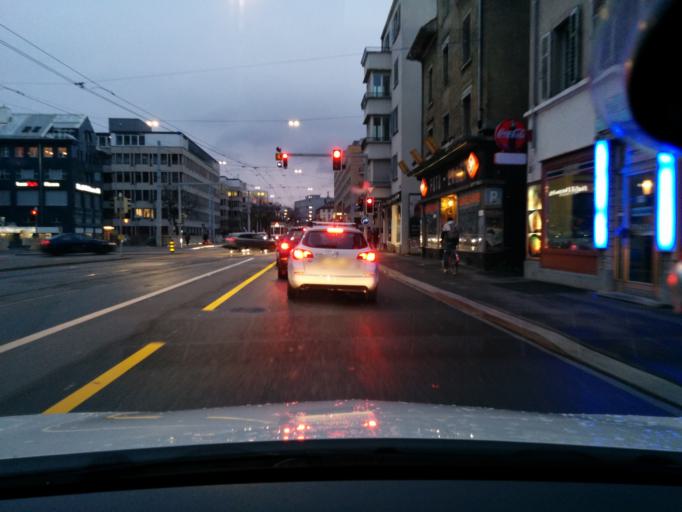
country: CH
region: Zurich
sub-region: Bezirk Zuerich
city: Aussersihl
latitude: 47.3753
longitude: 8.5180
